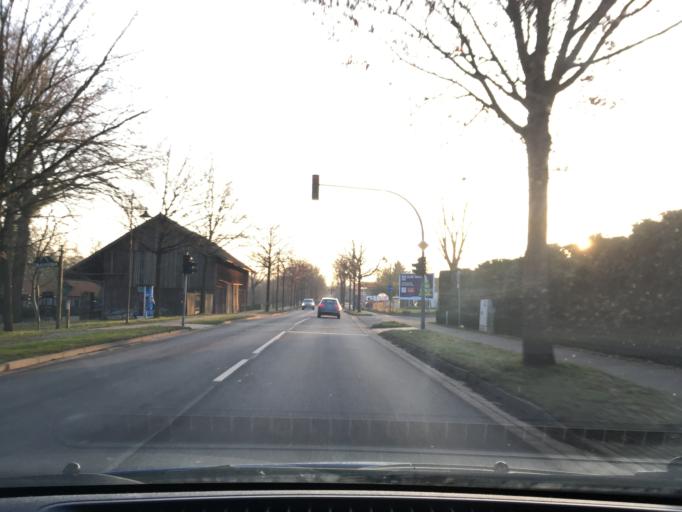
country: DE
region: Lower Saxony
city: Eschede
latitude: 52.7371
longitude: 10.2406
